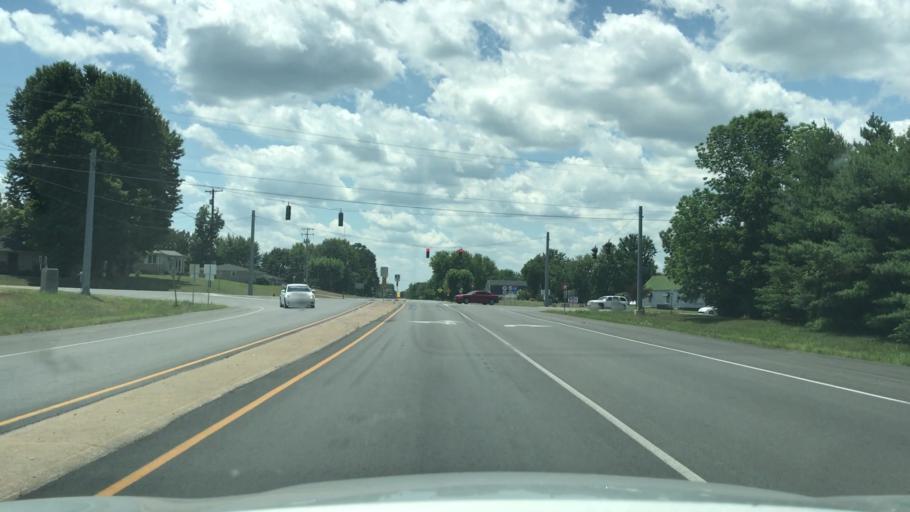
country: US
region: Kentucky
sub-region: Muhlenberg County
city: Greenville
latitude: 37.2005
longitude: -87.2049
